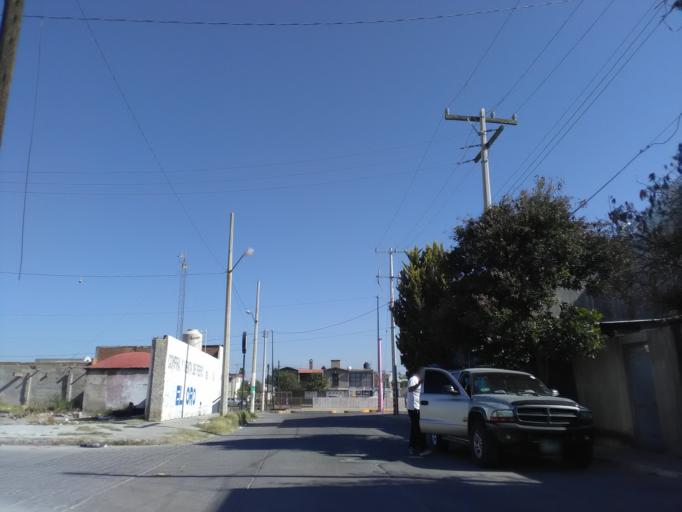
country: MX
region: Durango
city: Victoria de Durango
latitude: 24.0151
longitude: -104.6434
